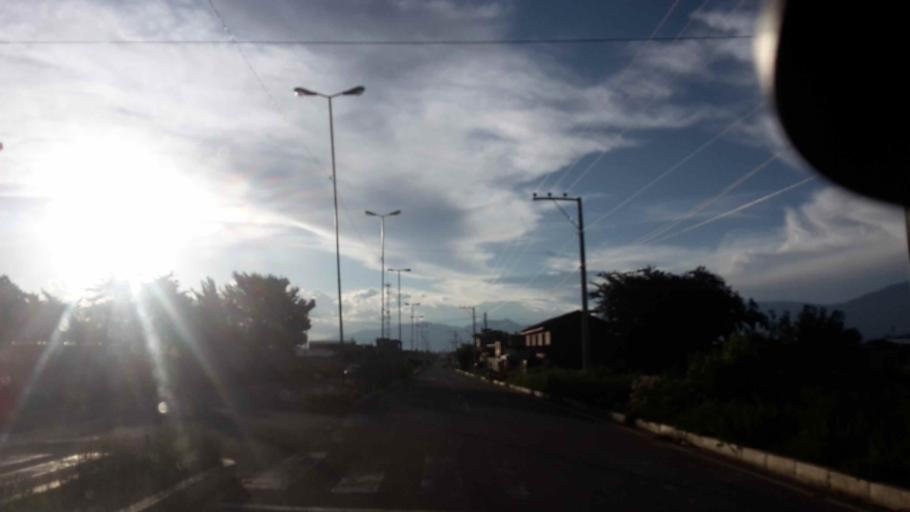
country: BO
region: Cochabamba
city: Arani
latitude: -17.5712
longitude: -65.7658
